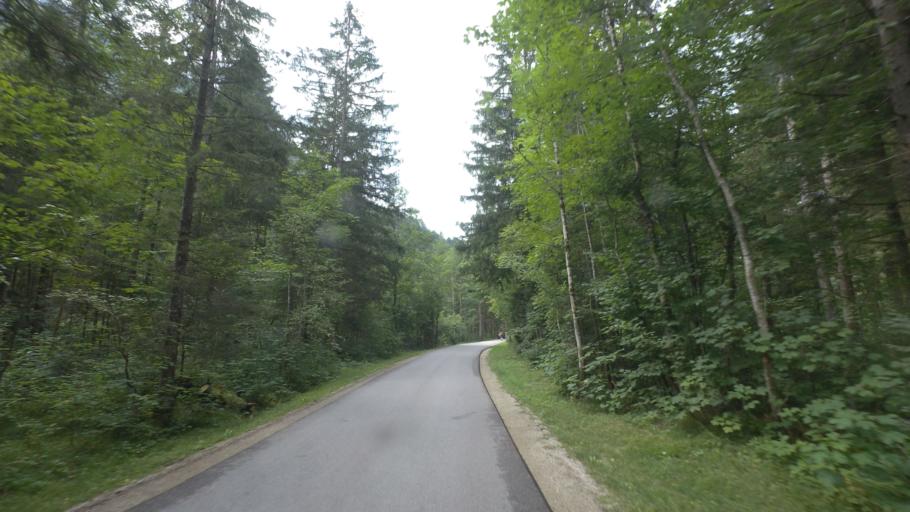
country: DE
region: Bavaria
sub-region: Upper Bavaria
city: Ruhpolding
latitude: 47.7295
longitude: 12.5862
